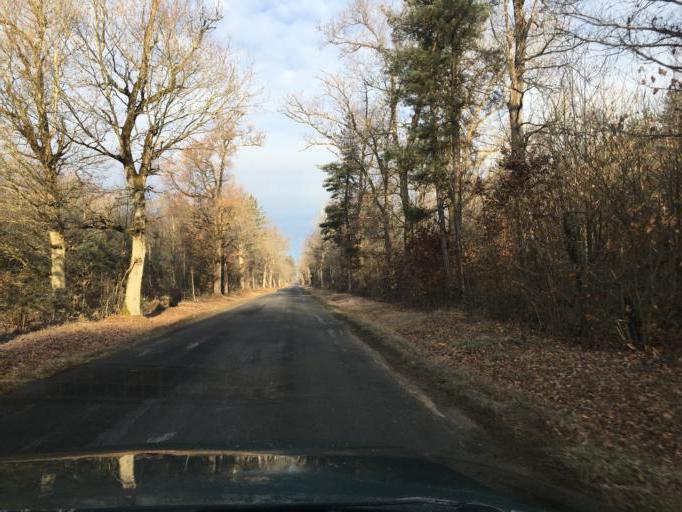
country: FR
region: Centre
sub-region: Departement du Loiret
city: Jouy-le-Potier
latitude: 47.8022
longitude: 1.8206
